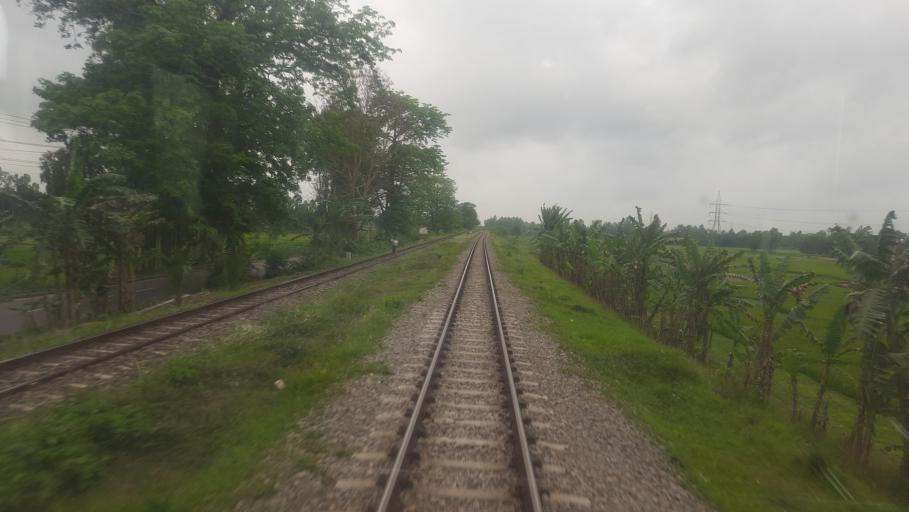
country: BD
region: Dhaka
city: Narsingdi
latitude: 23.9467
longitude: 90.7894
